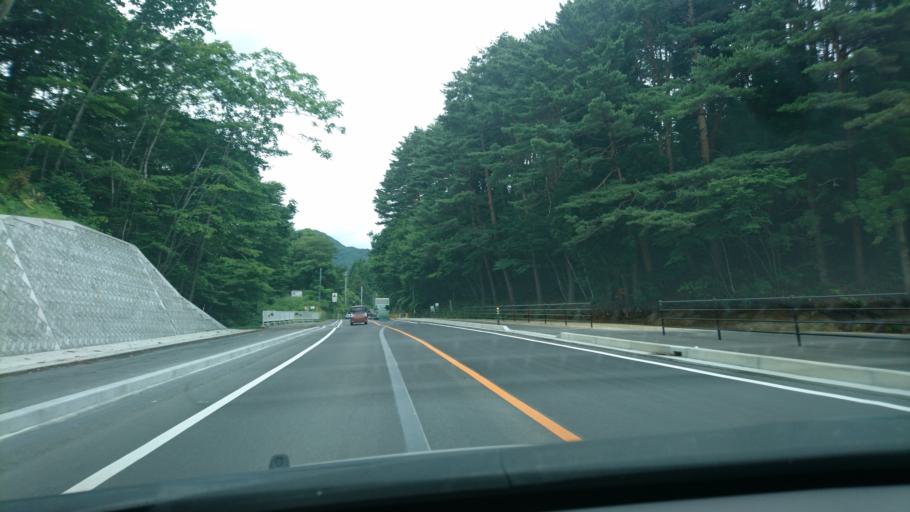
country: JP
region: Iwate
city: Otsuchi
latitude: 39.3756
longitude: 141.9420
